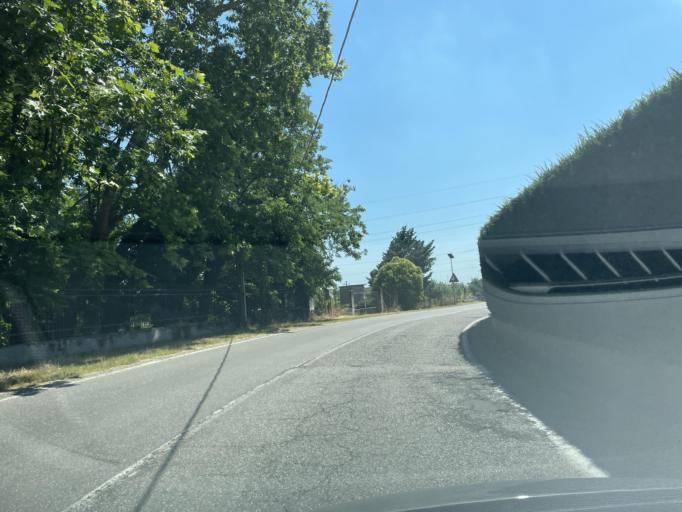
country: IT
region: Veneto
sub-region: Provincia di Verona
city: San Martino Buon Albergo
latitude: 45.4016
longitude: 11.0879
